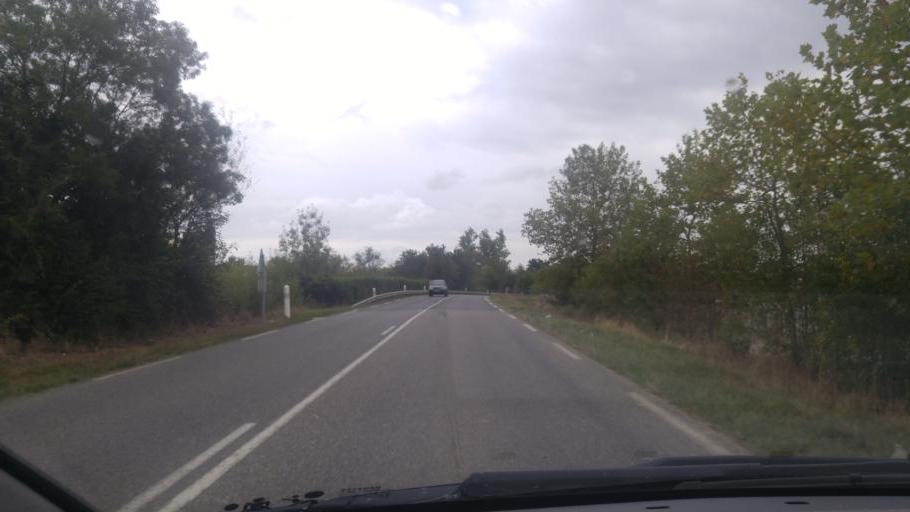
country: FR
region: Midi-Pyrenees
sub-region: Departement du Gers
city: Lectoure
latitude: 43.9161
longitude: 0.6287
